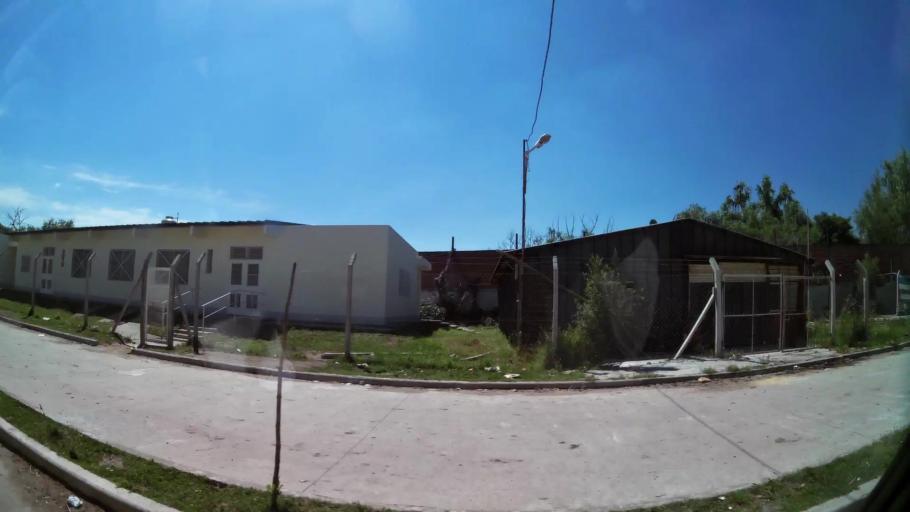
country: AR
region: Buenos Aires
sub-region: Partido de Tigre
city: Tigre
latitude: -34.4260
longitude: -58.5616
